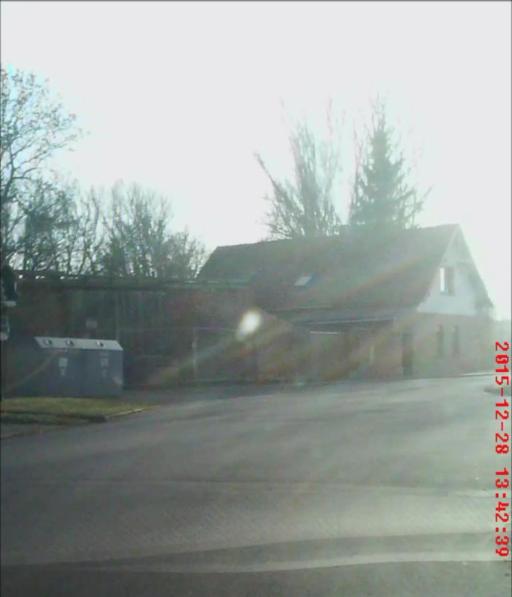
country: DE
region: Thuringia
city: Eberstedt
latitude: 51.0739
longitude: 11.5787
